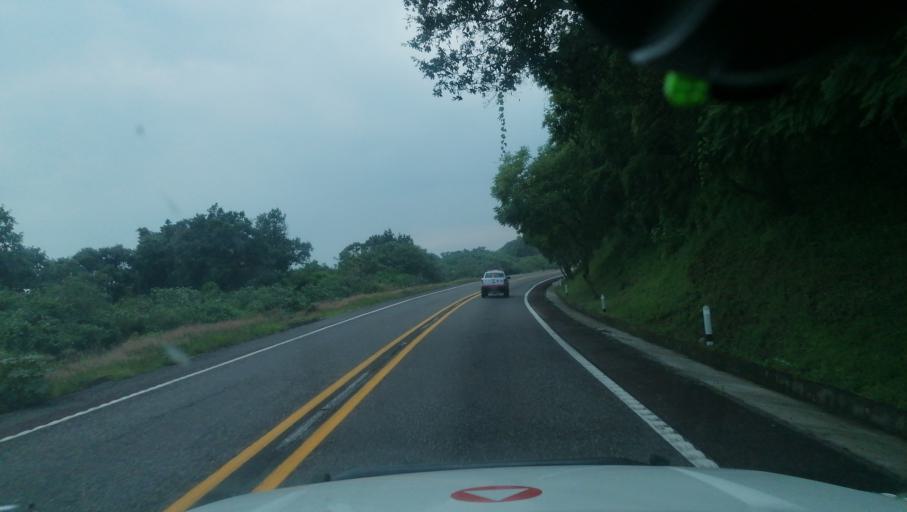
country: MX
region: Morelos
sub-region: Cuernavaca
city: Villa Santiago
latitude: 19.0089
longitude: -99.1621
